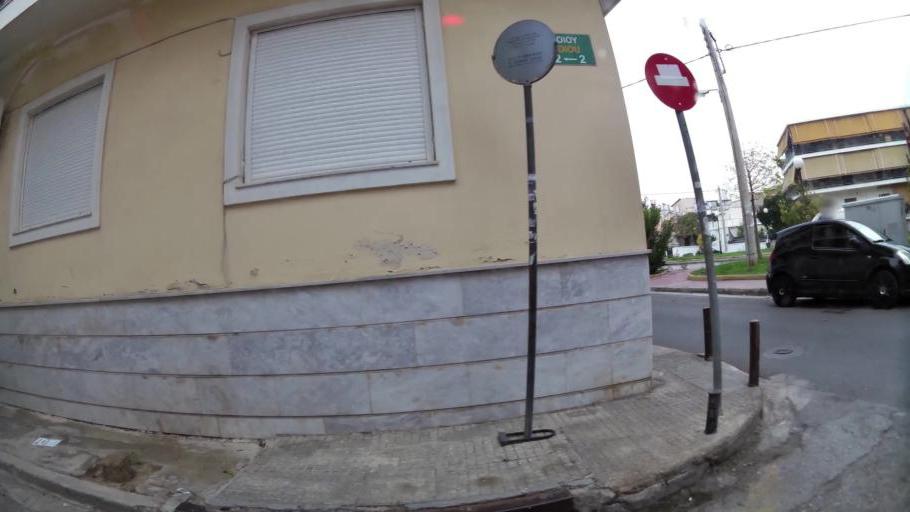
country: GR
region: Attica
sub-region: Nomarchia Athinas
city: Peristeri
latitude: 38.0013
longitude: 23.6920
